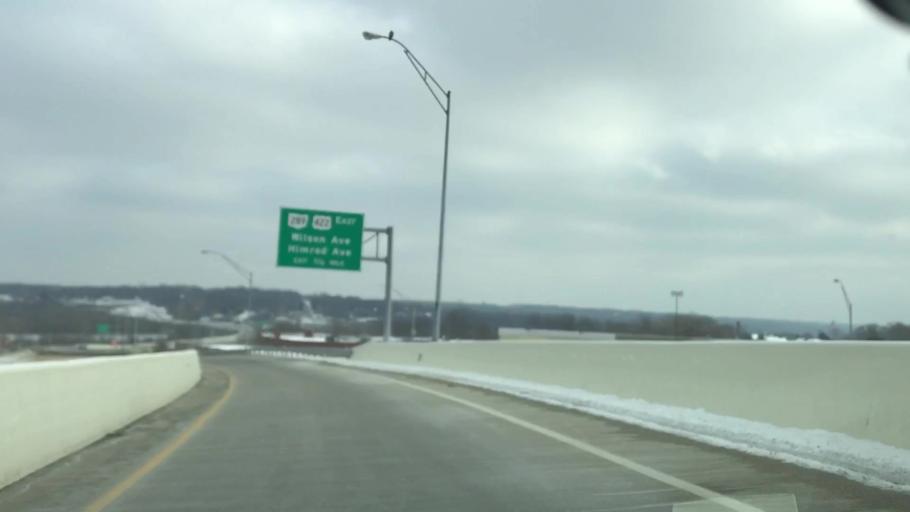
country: US
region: Ohio
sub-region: Mahoning County
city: Youngstown
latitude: 41.0912
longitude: -80.6501
